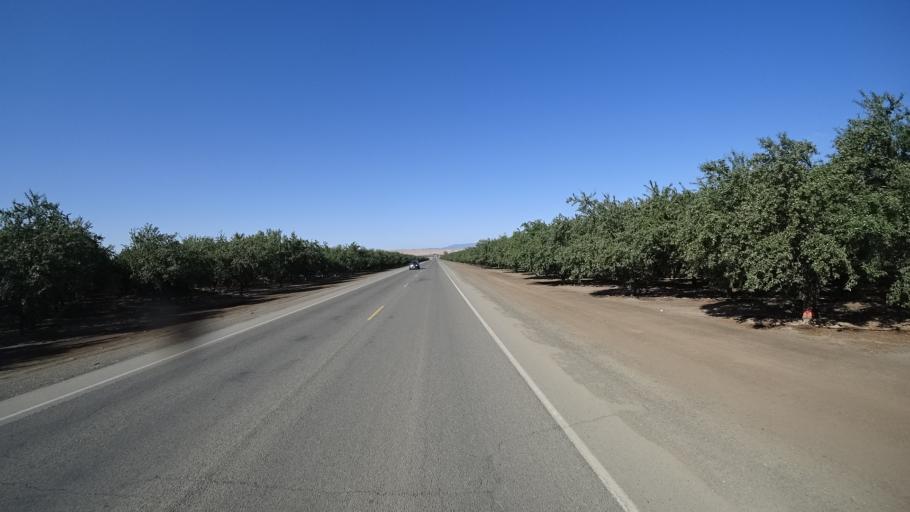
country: US
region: California
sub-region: Fresno County
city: Huron
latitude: 36.1079
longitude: -120.0495
